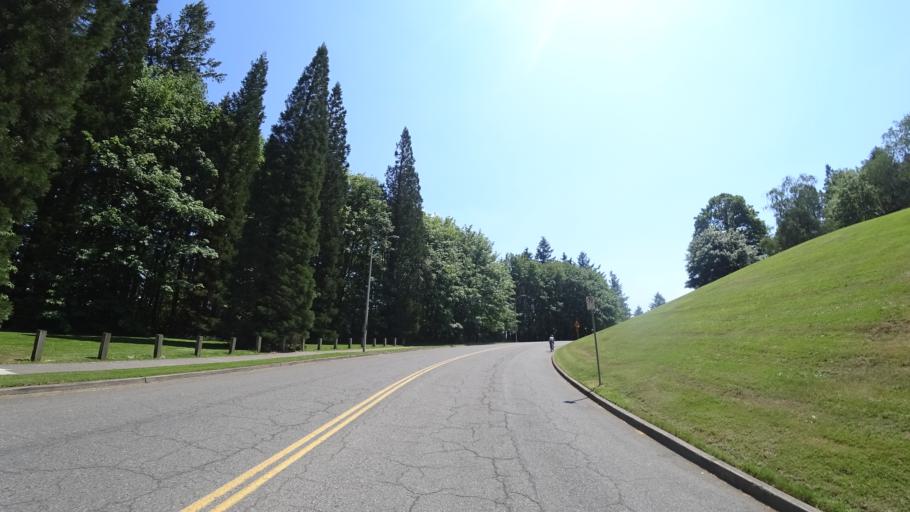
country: US
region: Oregon
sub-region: Multnomah County
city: Portland
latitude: 45.4990
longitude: -122.7054
